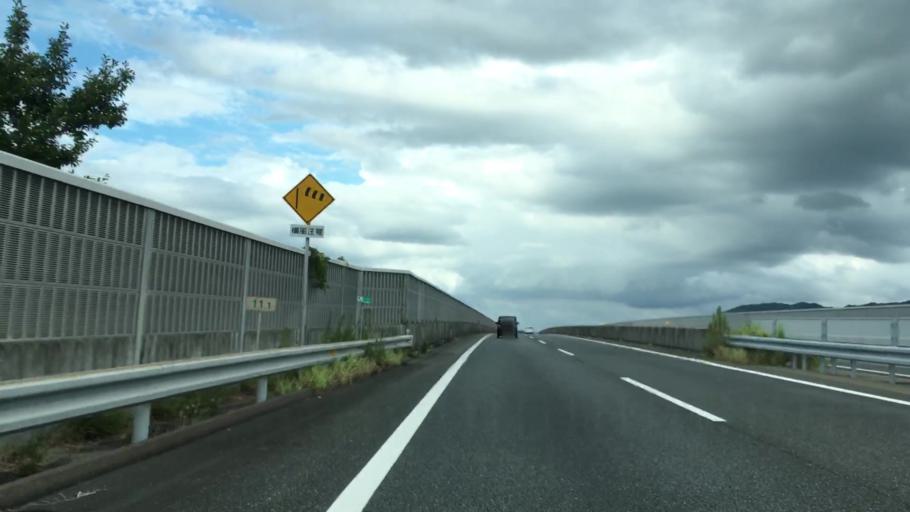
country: JP
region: Fukuoka
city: Maebaru-chuo
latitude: 33.5475
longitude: 130.2107
